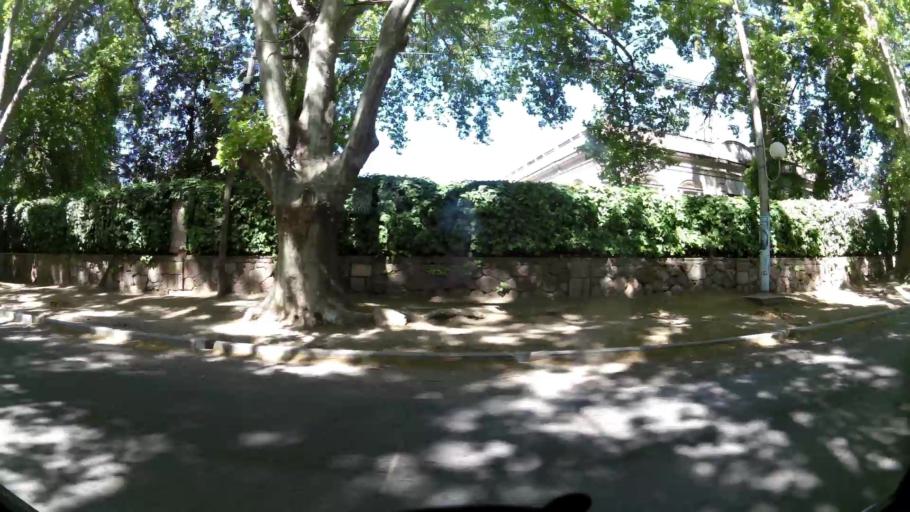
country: AR
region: Mendoza
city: Lujan de Cuyo
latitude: -32.9828
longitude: -68.8600
